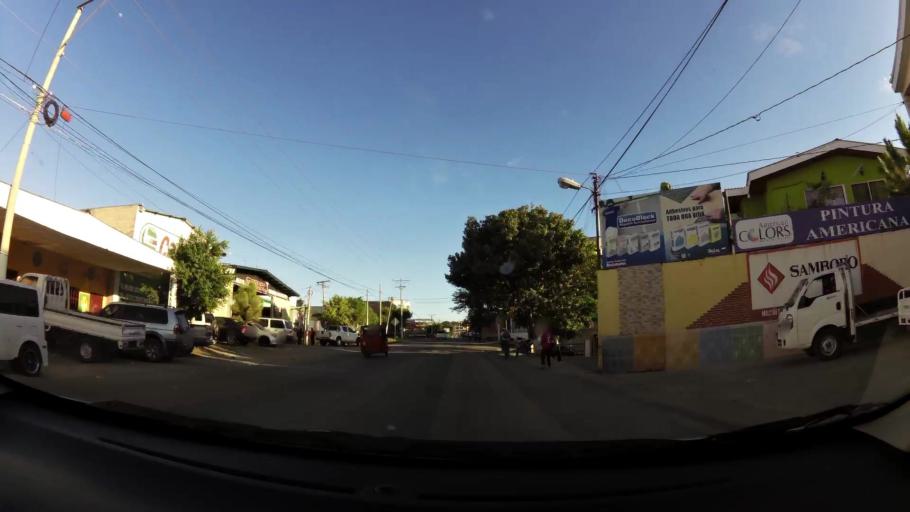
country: SV
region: Santa Ana
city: Metapan
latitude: 14.3350
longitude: -89.4454
